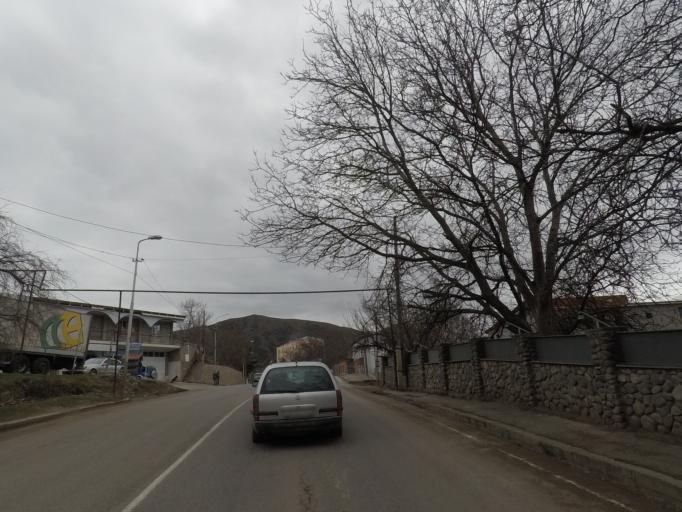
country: GE
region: Samtskhe-Javakheti
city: Aspindza
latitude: 41.5704
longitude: 43.2540
